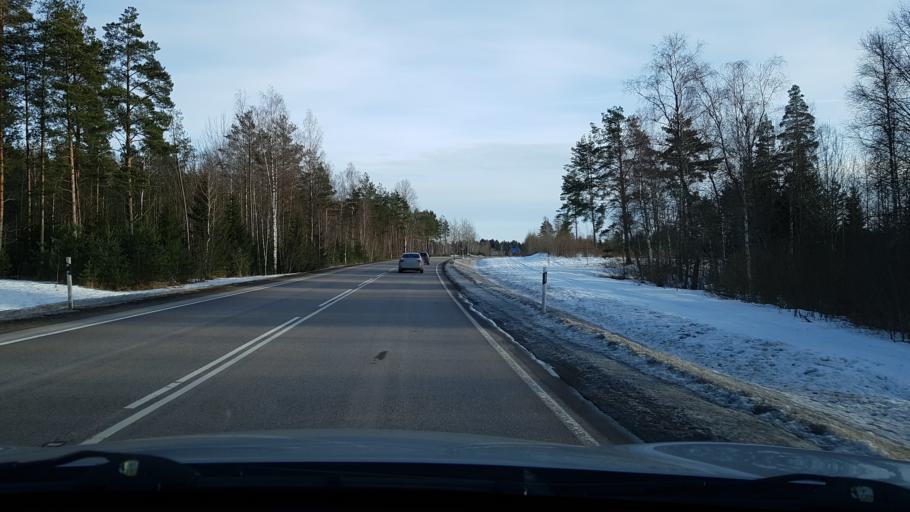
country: EE
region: Tartu
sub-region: Puhja vald
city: Puhja
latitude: 58.4120
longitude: 26.0709
